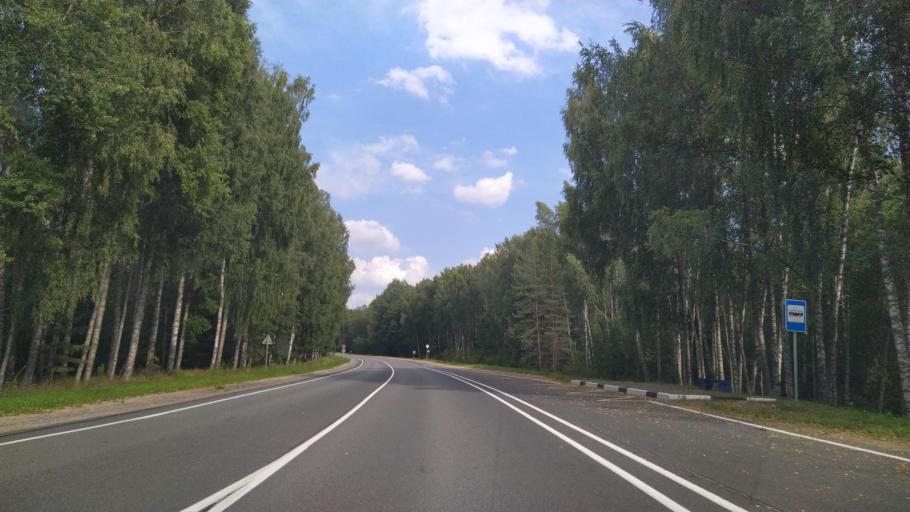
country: RU
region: Pskov
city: Dno
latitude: 57.9828
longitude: 29.7900
